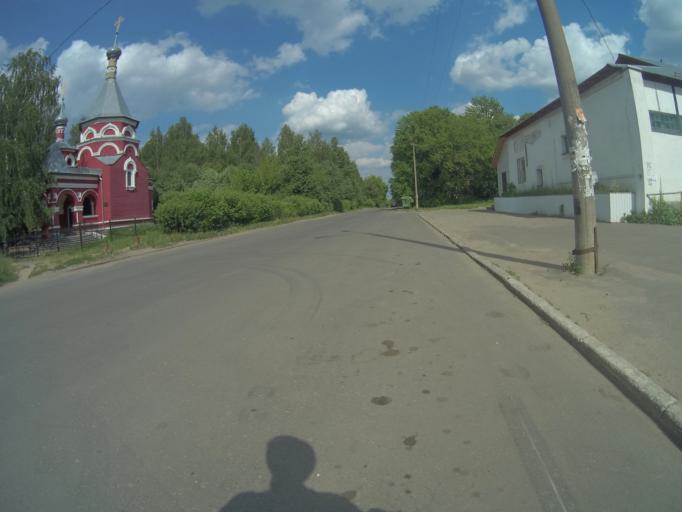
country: RU
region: Vladimir
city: Suzdal'
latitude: 56.4416
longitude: 40.4577
